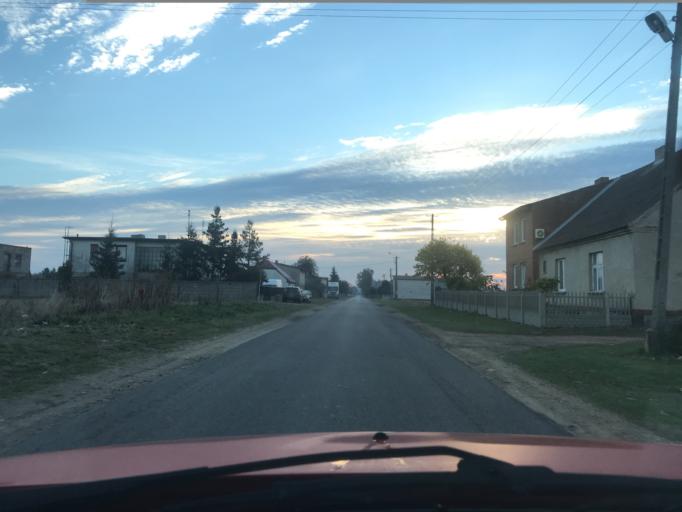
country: PL
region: Greater Poland Voivodeship
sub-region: Powiat ostrowski
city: Raszkow
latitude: 51.7195
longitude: 17.7803
